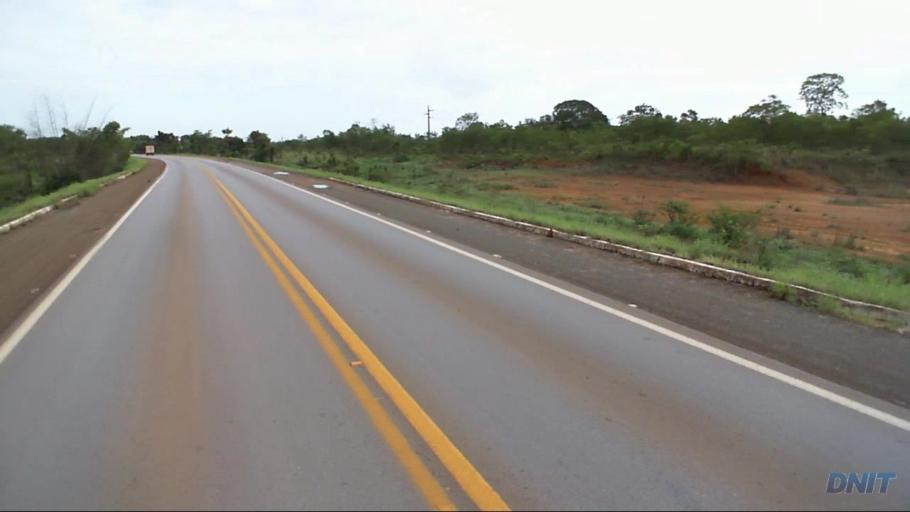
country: BR
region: Goias
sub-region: Uruacu
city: Uruacu
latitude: -14.7386
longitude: -49.0842
